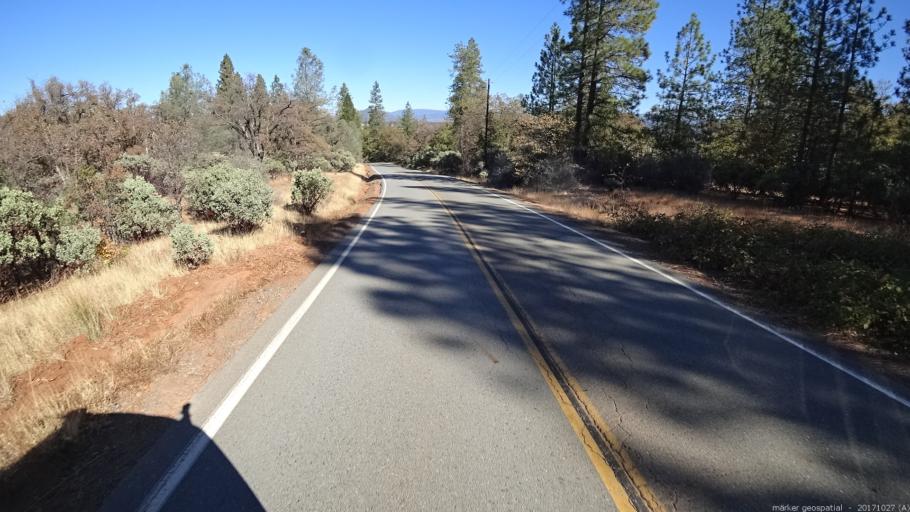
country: US
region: California
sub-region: Shasta County
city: Bella Vista
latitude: 40.7245
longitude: -122.0220
